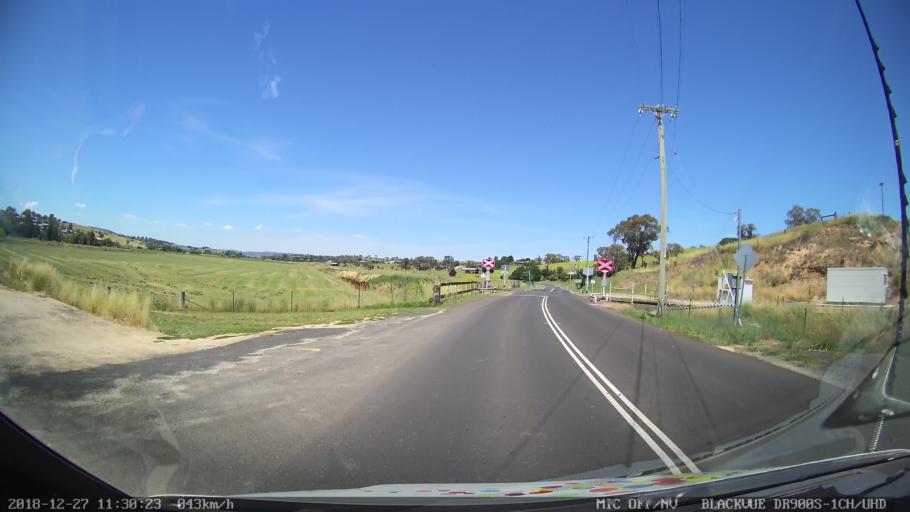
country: AU
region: New South Wales
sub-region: Bathurst Regional
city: Perthville
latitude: -33.4872
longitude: 149.5461
